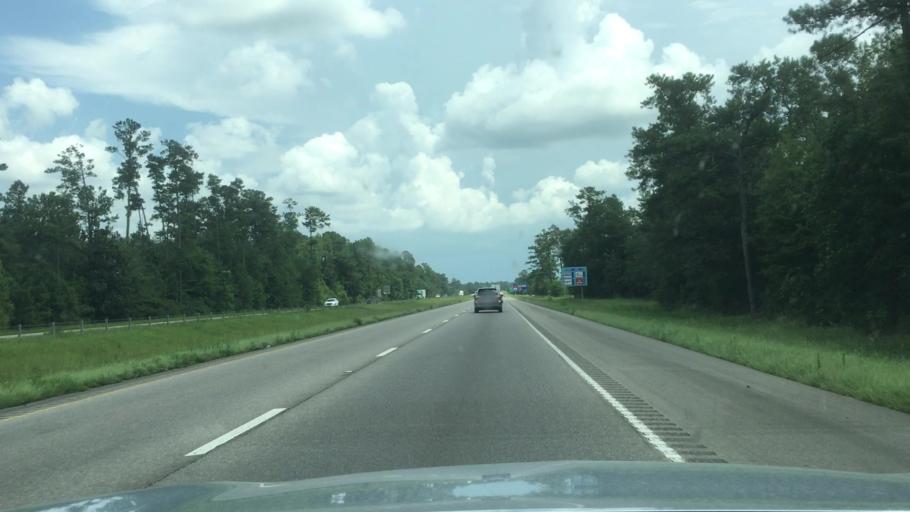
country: US
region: Mississippi
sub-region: Pearl River County
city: Picayune
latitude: 30.5059
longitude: -89.6673
